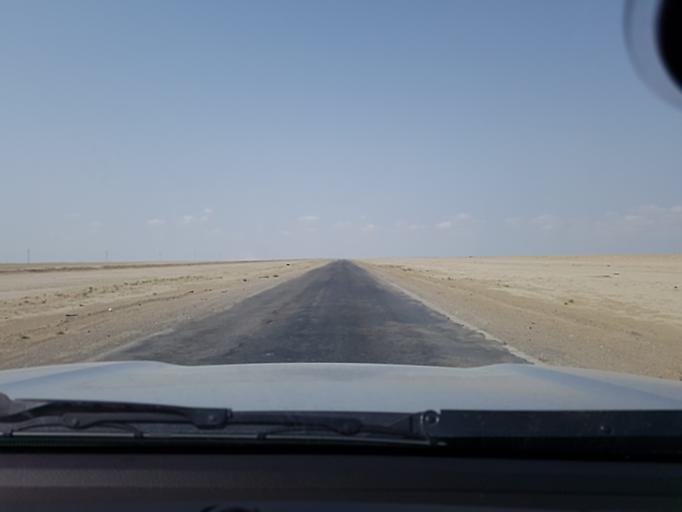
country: TM
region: Balkan
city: Gumdag
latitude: 38.6794
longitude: 54.4144
